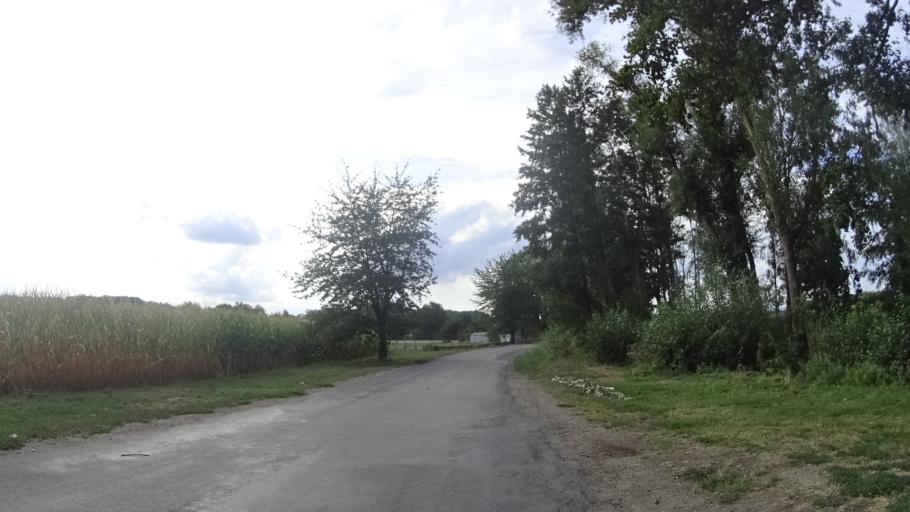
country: CZ
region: Olomoucky
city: Dubicko
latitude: 49.7970
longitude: 16.9598
